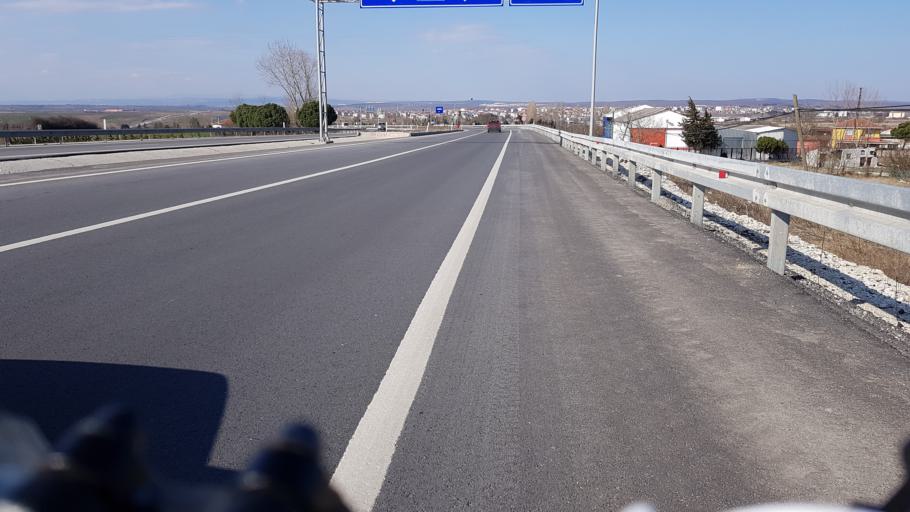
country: TR
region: Tekirdag
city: Saray
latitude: 41.4153
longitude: 27.9224
